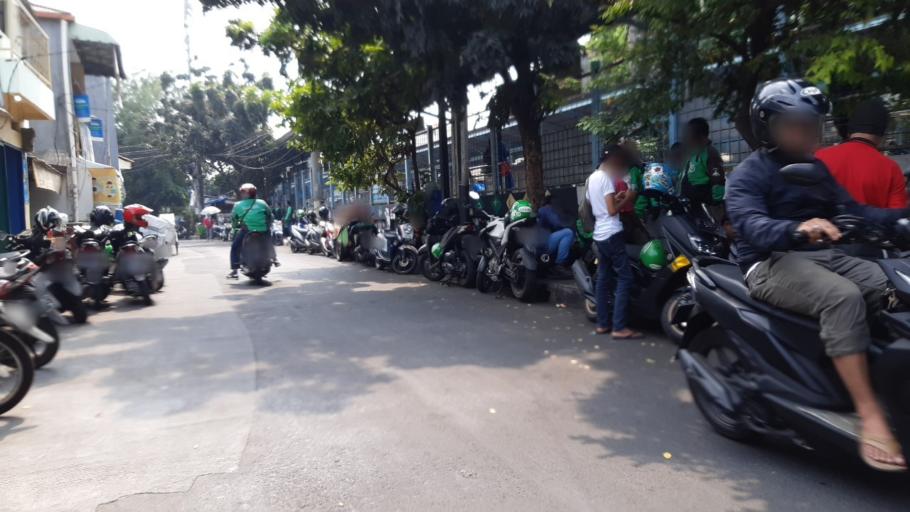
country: ID
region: Jakarta Raya
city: Jakarta
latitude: -6.2274
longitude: 106.8584
